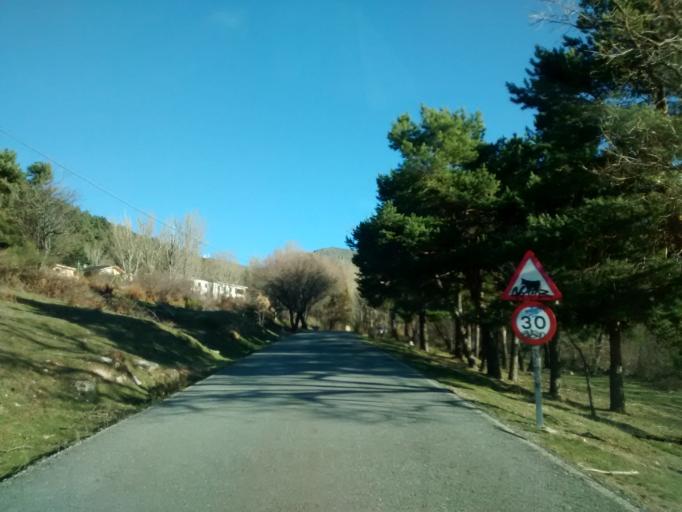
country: ES
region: Madrid
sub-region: Provincia de Madrid
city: Navacerrada
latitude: 40.7420
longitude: -4.0035
